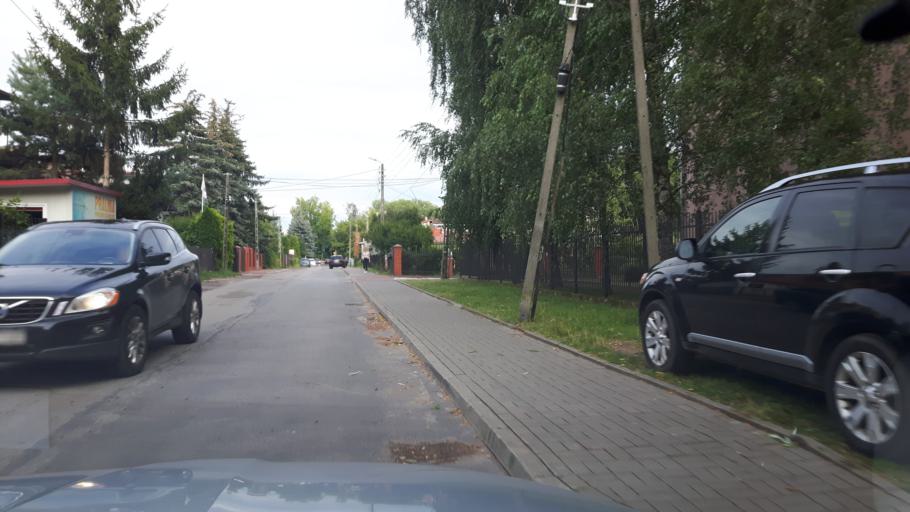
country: PL
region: Masovian Voivodeship
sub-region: Powiat wolominski
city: Marki
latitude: 52.3281
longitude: 21.1048
